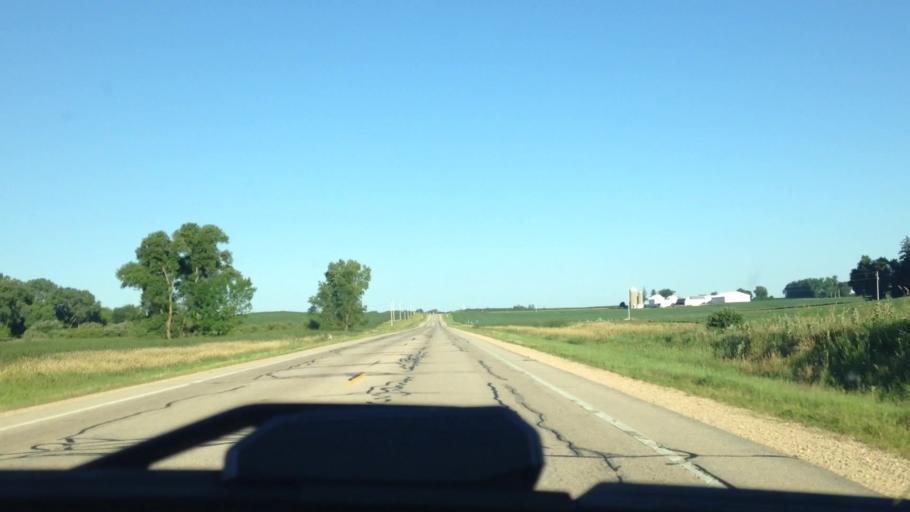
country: US
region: Wisconsin
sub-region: Columbia County
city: Rio
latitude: 43.3400
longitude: -89.2334
